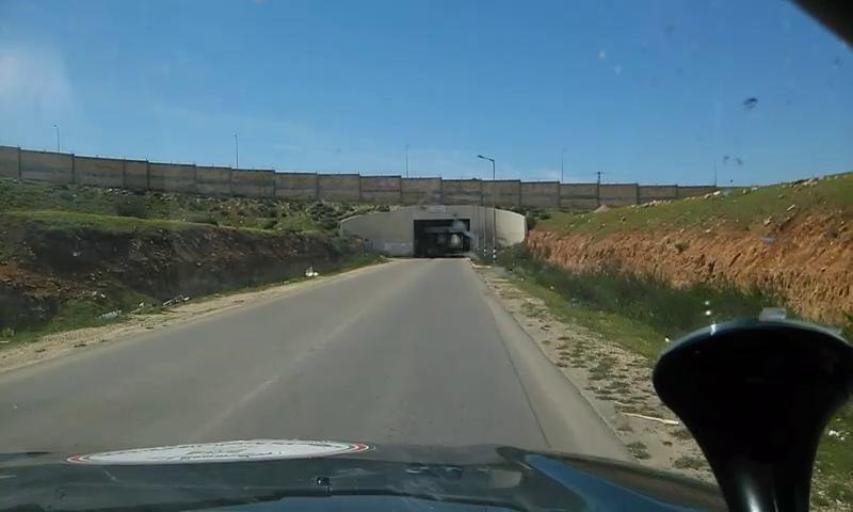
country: IL
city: Giv'on HaHadasha
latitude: 31.8423
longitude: 35.1733
